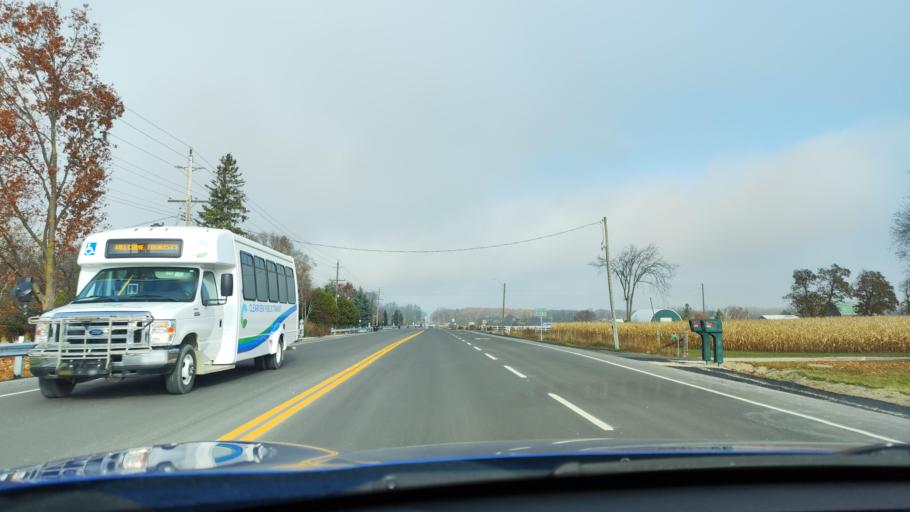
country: CA
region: Ontario
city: Wasaga Beach
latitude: 44.4554
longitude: -80.0714
